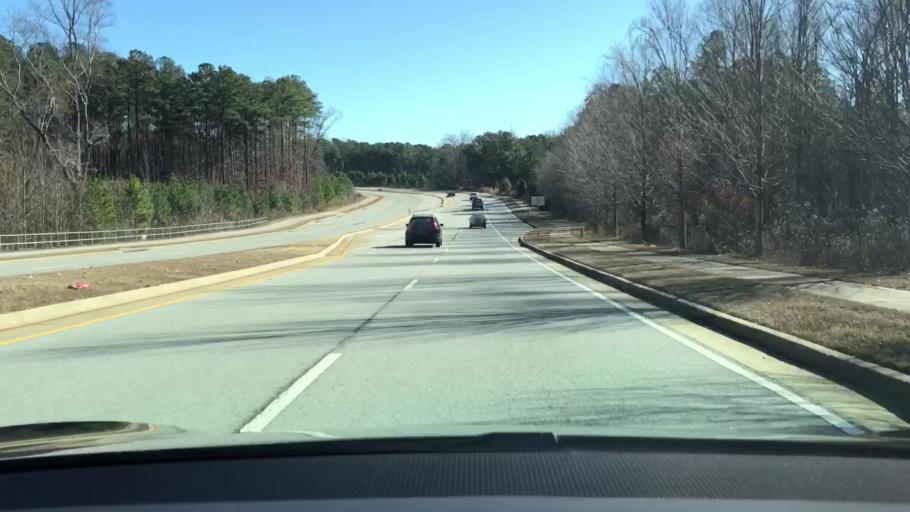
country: US
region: Georgia
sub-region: Gwinnett County
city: Suwanee
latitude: 34.0217
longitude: -84.0493
